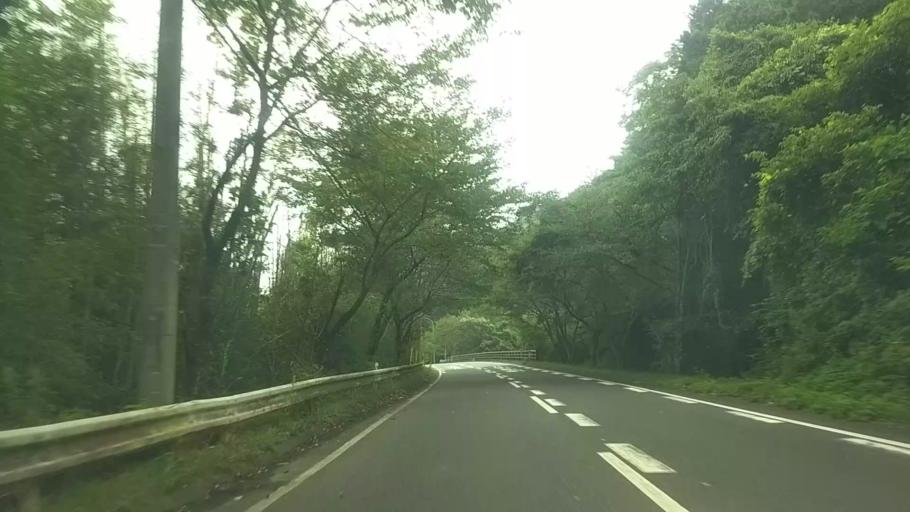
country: JP
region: Chiba
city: Kimitsu
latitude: 35.2304
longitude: 139.9649
